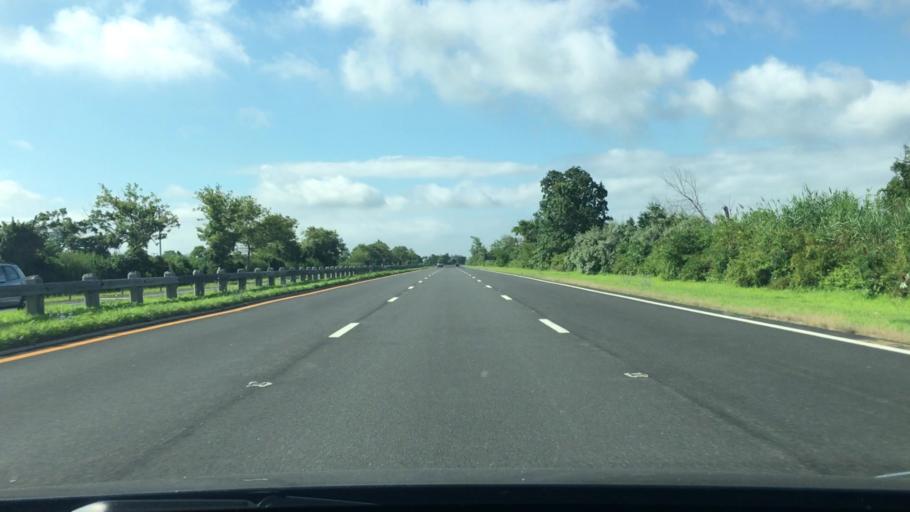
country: US
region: New York
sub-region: Nassau County
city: Bellmore
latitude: 40.6539
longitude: -73.5100
